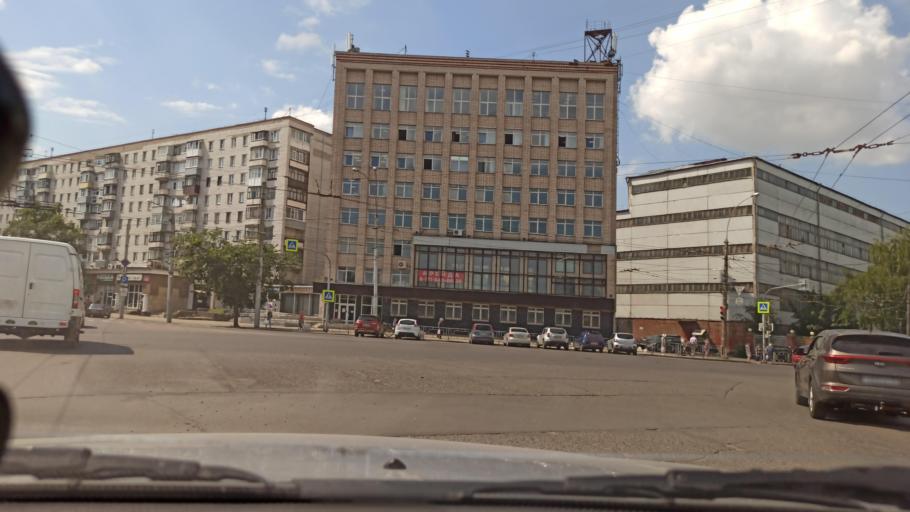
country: RU
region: Vologda
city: Vologda
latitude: 59.2182
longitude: 39.8836
